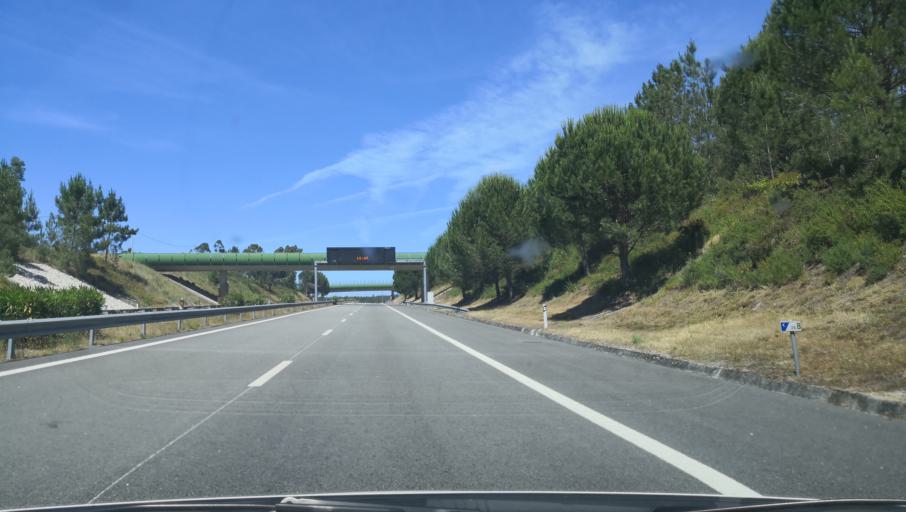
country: PT
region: Coimbra
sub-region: Montemor-O-Velho
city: Arazede
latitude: 40.2300
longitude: -8.6676
